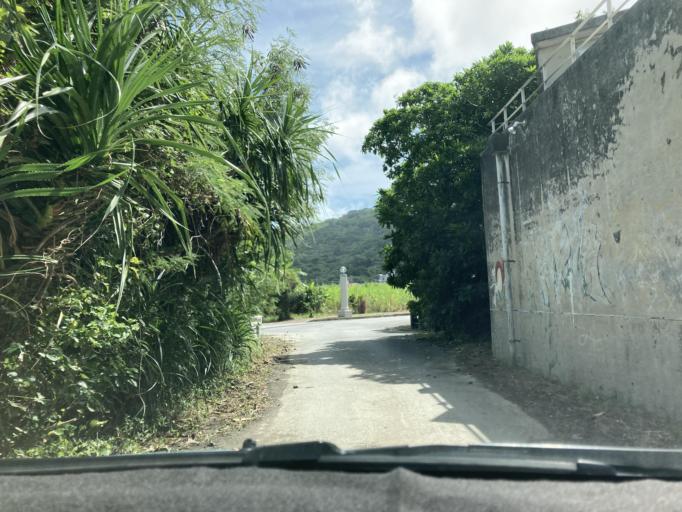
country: JP
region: Okinawa
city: Ginowan
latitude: 26.1704
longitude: 127.7881
